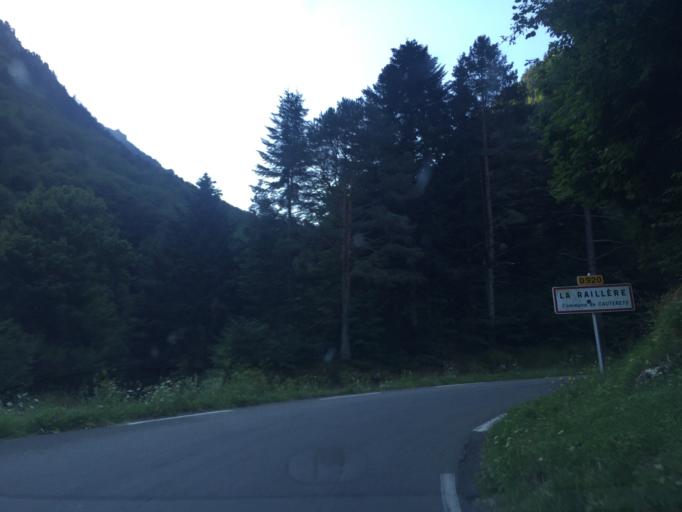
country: FR
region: Midi-Pyrenees
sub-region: Departement des Hautes-Pyrenees
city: Cauterets
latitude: 42.8741
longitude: -0.1088
